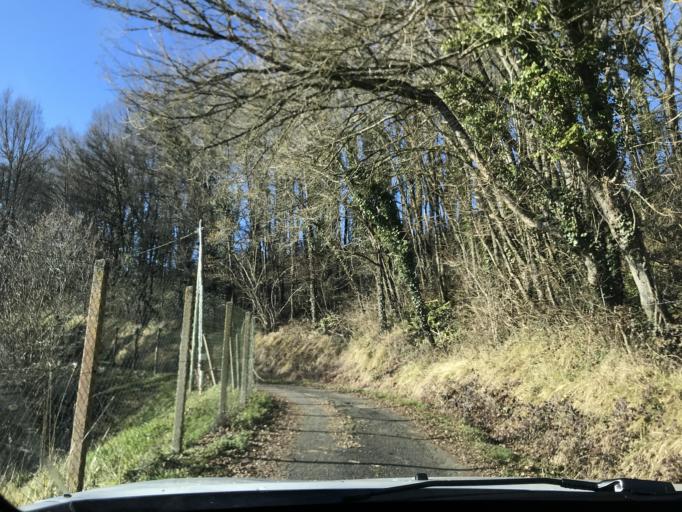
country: FR
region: Poitou-Charentes
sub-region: Departement de la Charente
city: Chasseneuil-sur-Bonnieure
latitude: 45.8358
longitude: 0.5328
